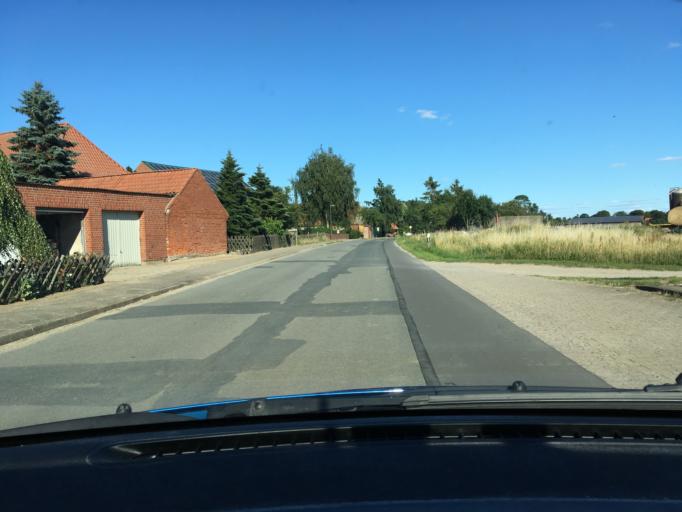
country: DE
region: Mecklenburg-Vorpommern
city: Boizenburg
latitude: 53.3480
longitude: 10.7161
